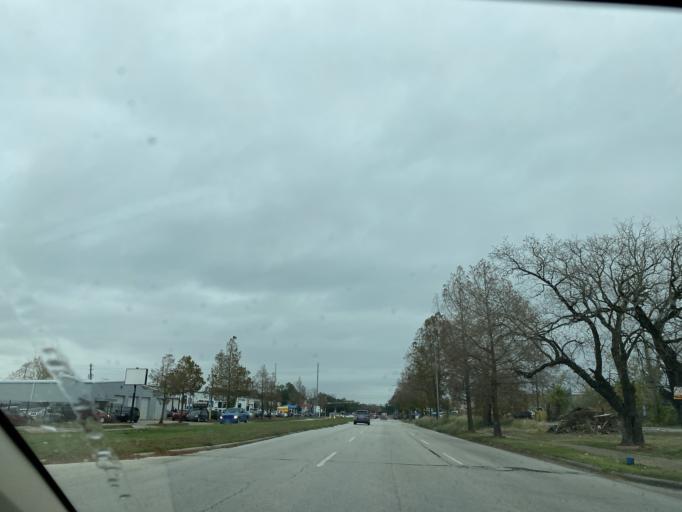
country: US
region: Texas
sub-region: Harris County
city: Piney Point Village
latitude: 29.7292
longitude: -95.5169
